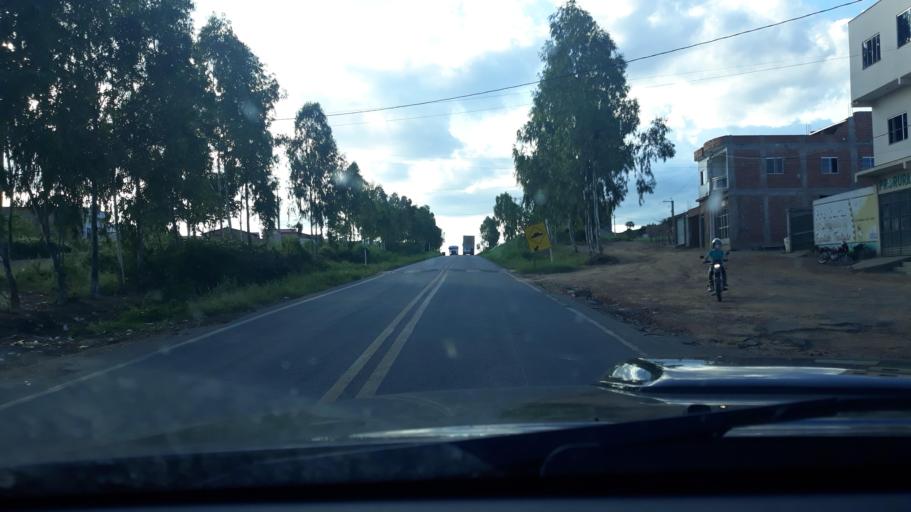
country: BR
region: Bahia
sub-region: Riacho De Santana
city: Riacho de Santana
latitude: -13.7673
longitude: -42.7211
